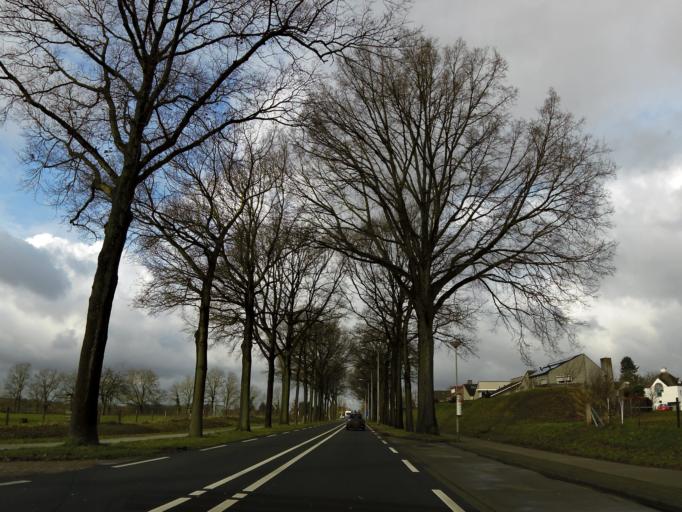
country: NL
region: Limburg
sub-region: Valkenburg aan de Geul
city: Berg
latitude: 50.8253
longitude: 5.7741
